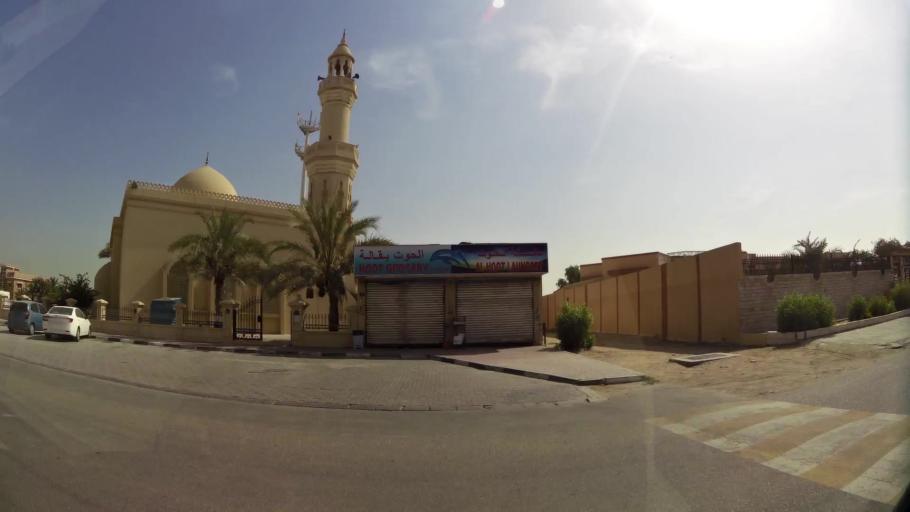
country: AE
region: Ash Shariqah
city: Sharjah
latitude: 25.2683
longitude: 55.4025
